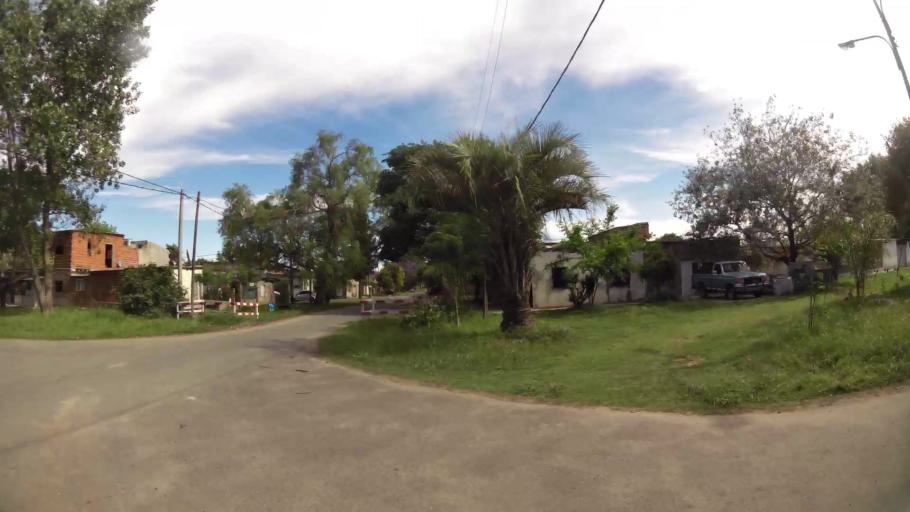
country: AR
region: Santa Fe
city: Granadero Baigorria
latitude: -32.9245
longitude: -60.7169
